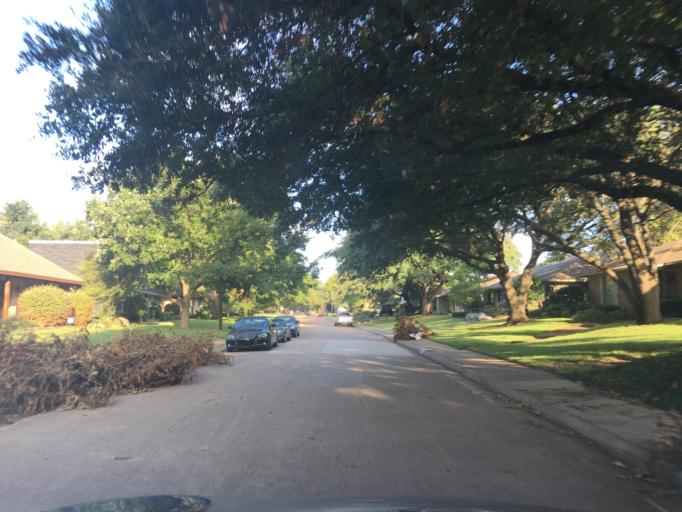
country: US
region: Texas
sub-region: Dallas County
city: Highland Park
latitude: 32.8501
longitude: -96.7559
